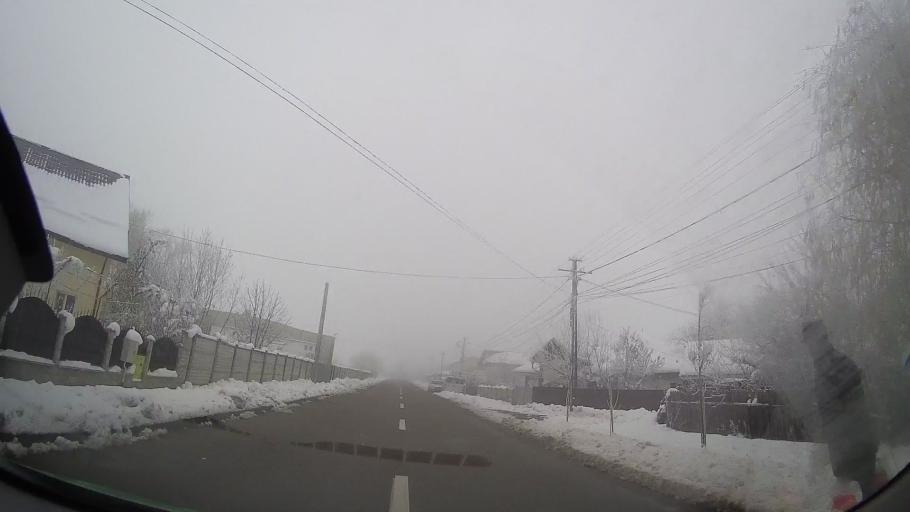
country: RO
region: Iasi
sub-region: Municipiul Pascani
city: Pascani
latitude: 47.2582
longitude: 26.7185
